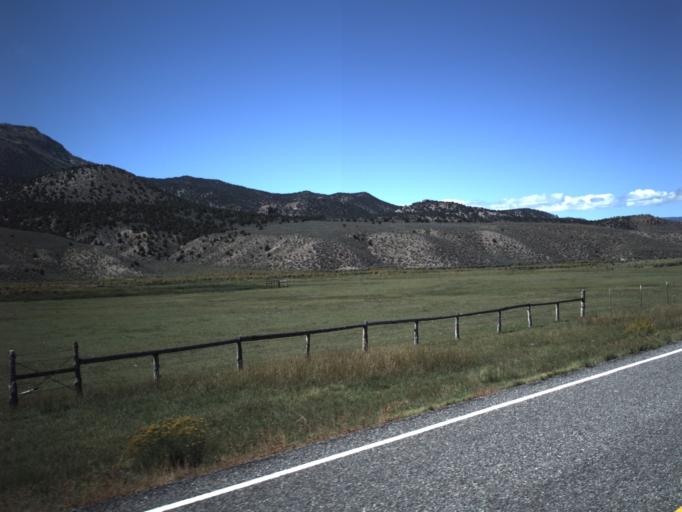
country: US
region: Utah
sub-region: Piute County
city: Junction
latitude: 38.1708
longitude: -112.0587
